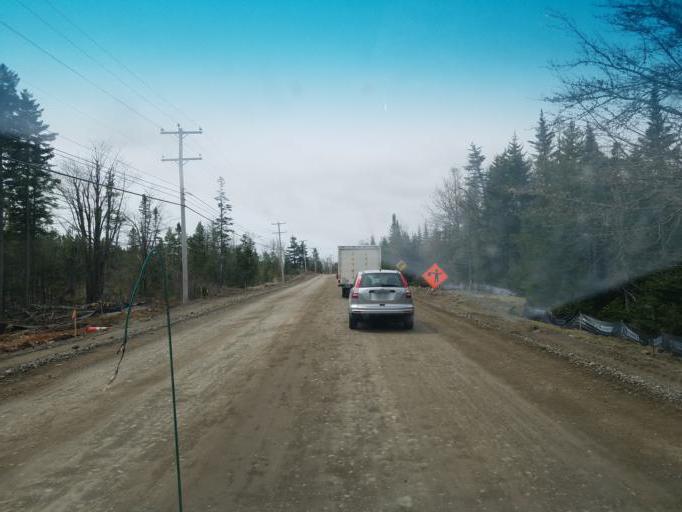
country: US
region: Maine
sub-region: Washington County
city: East Machias
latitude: 44.7712
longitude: -67.1967
